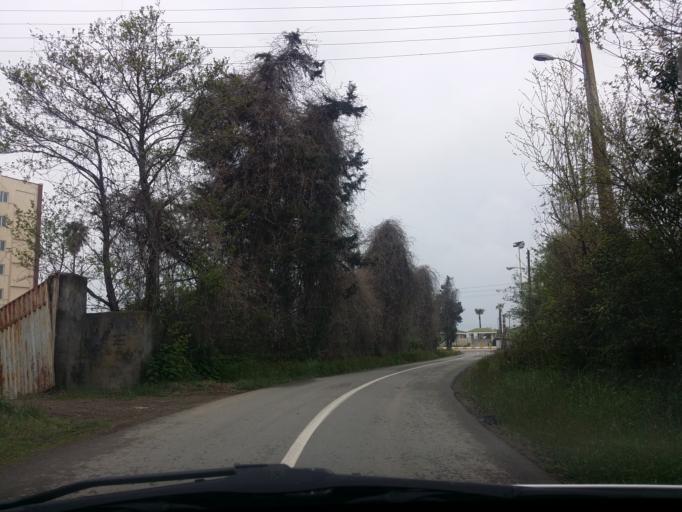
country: IR
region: Mazandaran
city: Chalus
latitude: 36.6863
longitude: 51.3795
